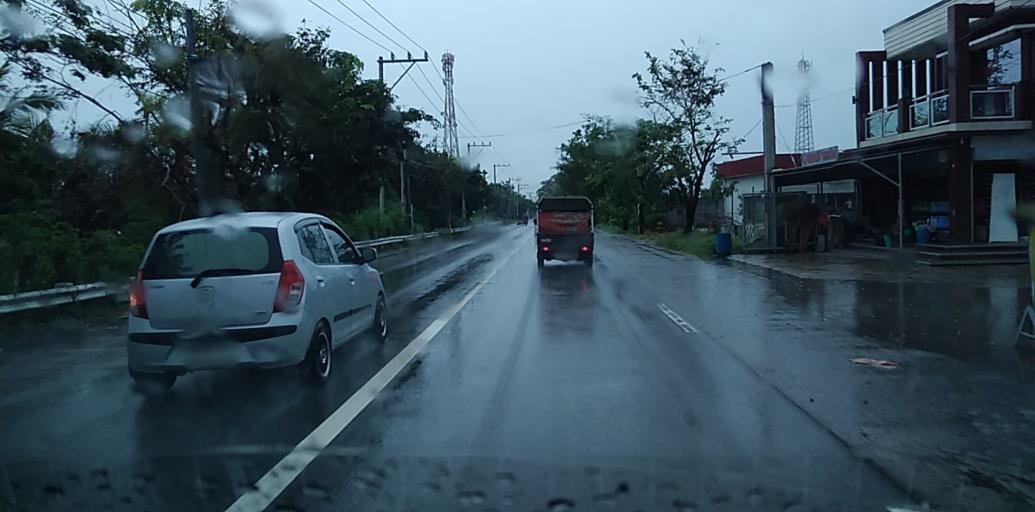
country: PH
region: Central Luzon
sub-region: Province of Bulacan
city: Bulualto
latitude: 15.2160
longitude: 120.9549
